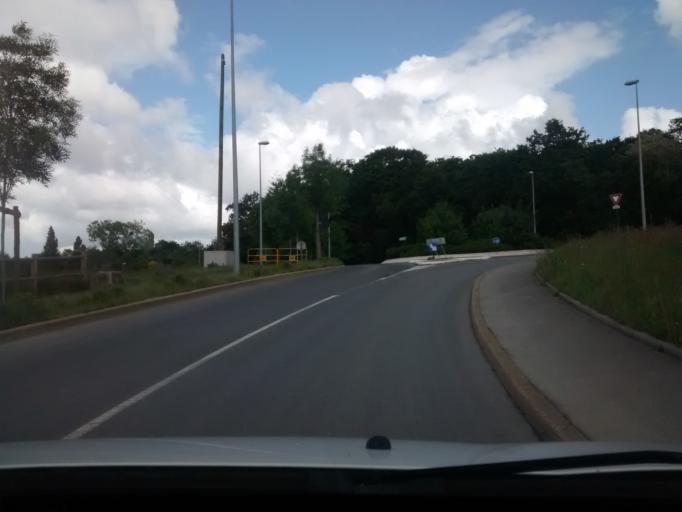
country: FR
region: Brittany
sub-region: Departement d'Ille-et-Vilaine
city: Cesson-Sevigne
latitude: 48.1079
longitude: -1.5997
